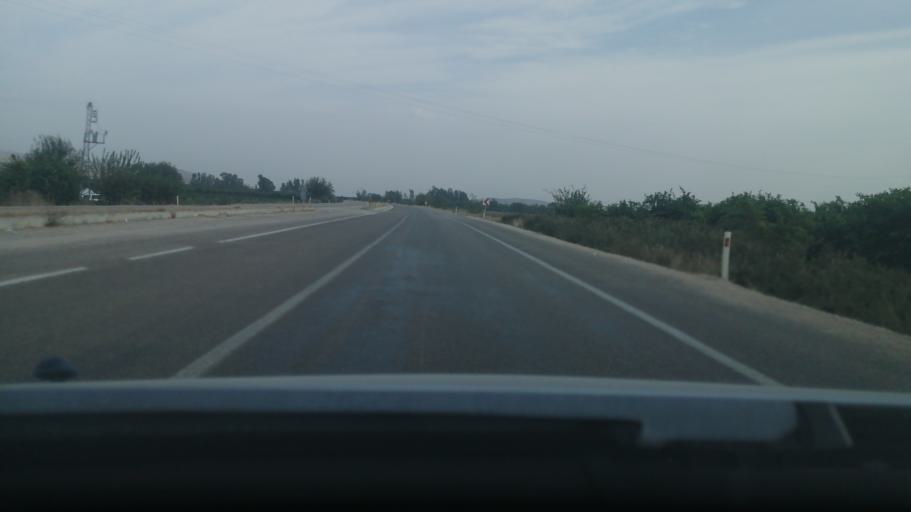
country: TR
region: Adana
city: Kozan
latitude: 37.3895
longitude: 35.7941
